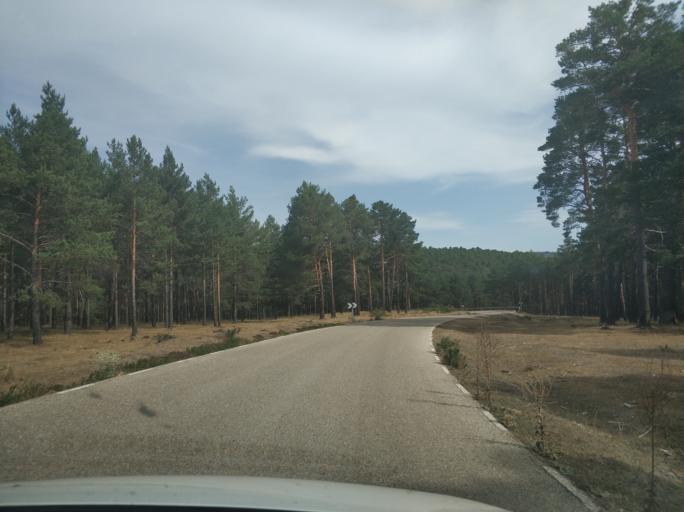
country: ES
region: Castille and Leon
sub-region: Provincia de Soria
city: Navaleno
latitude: 41.8612
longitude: -2.9400
